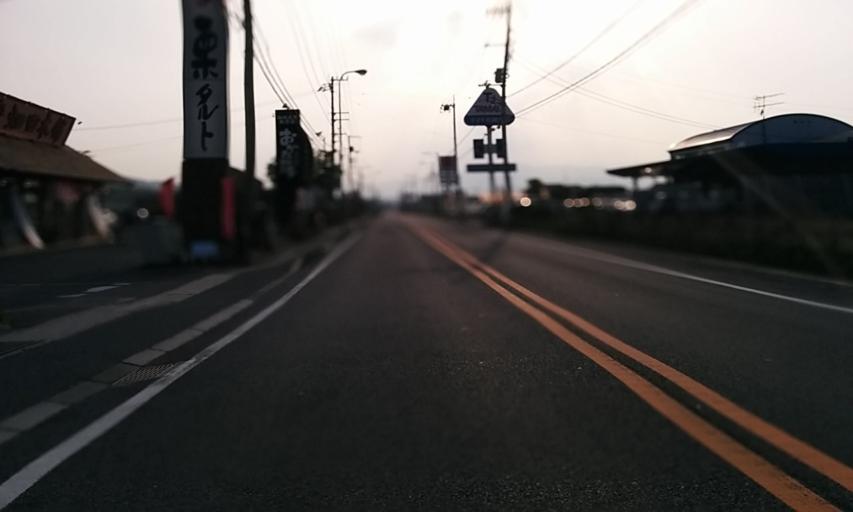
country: JP
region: Ehime
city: Saijo
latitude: 33.8952
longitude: 133.1643
